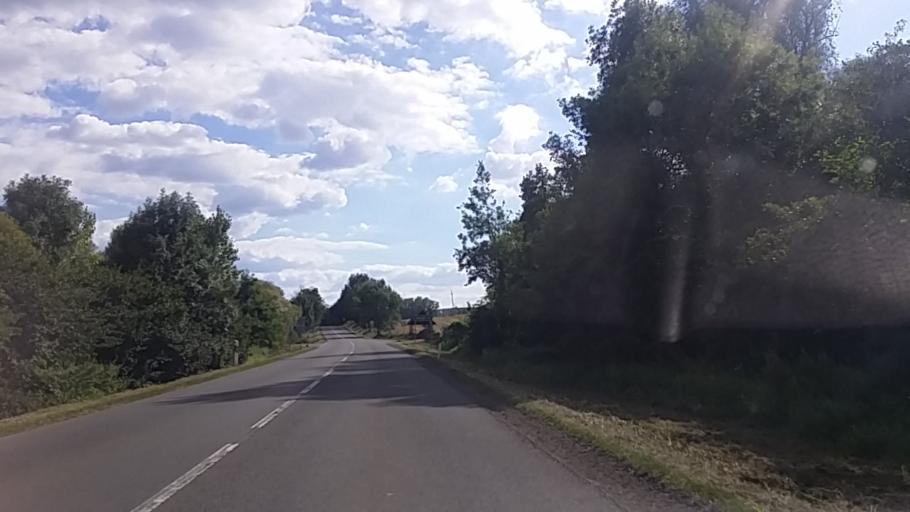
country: HU
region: Baranya
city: Sasd
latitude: 46.2796
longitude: 18.1087
